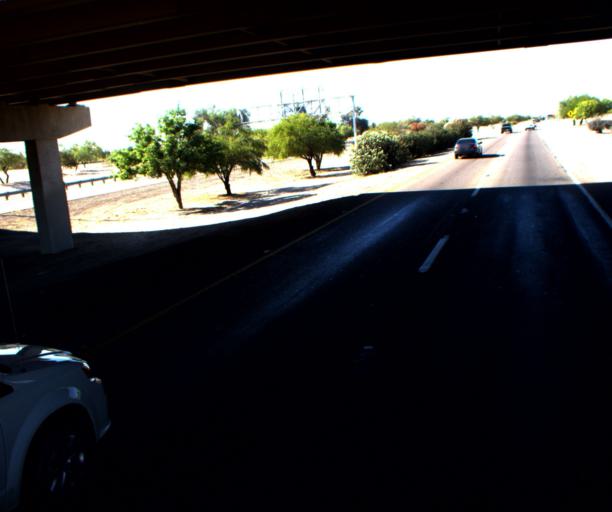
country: US
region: Arizona
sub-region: Pima County
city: South Tucson
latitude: 32.1634
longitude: -110.9858
